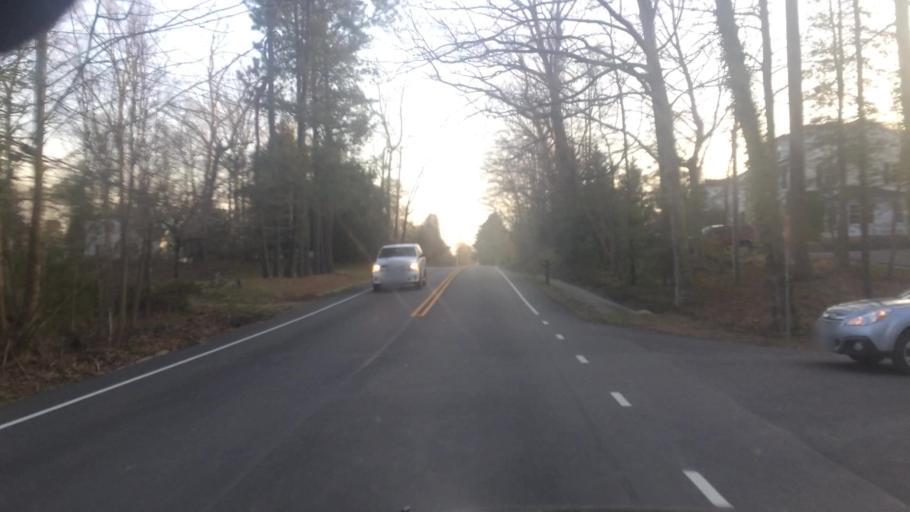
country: US
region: Virginia
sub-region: James City County
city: Williamsburg
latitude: 37.2454
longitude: -76.7401
